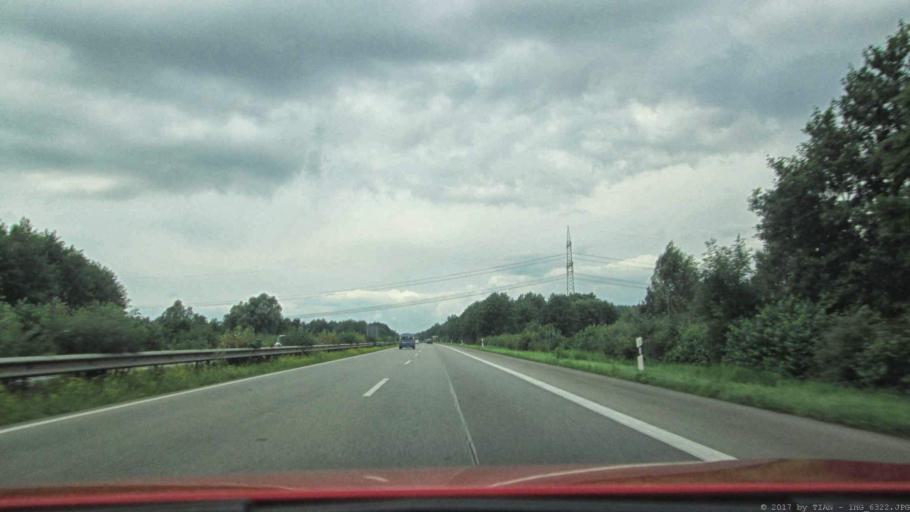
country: DE
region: Lower Saxony
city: Mechtersen
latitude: 53.3133
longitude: 10.3213
